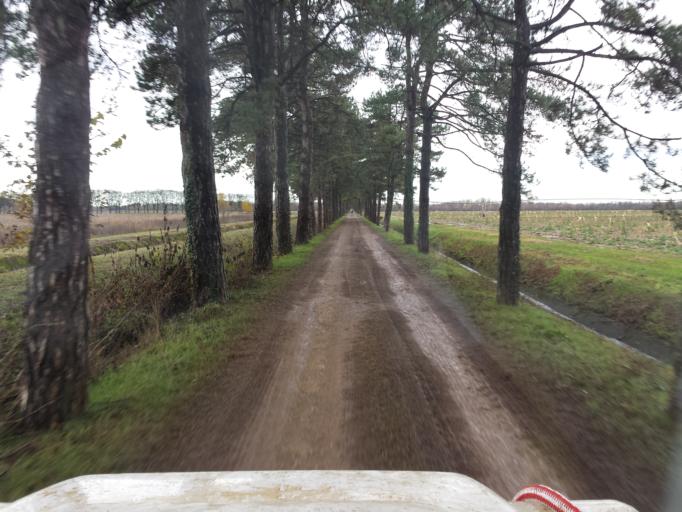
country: IT
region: Friuli Venezia Giulia
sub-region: Provincia di Gorizia
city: Medea
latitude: 45.9397
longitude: 13.4366
